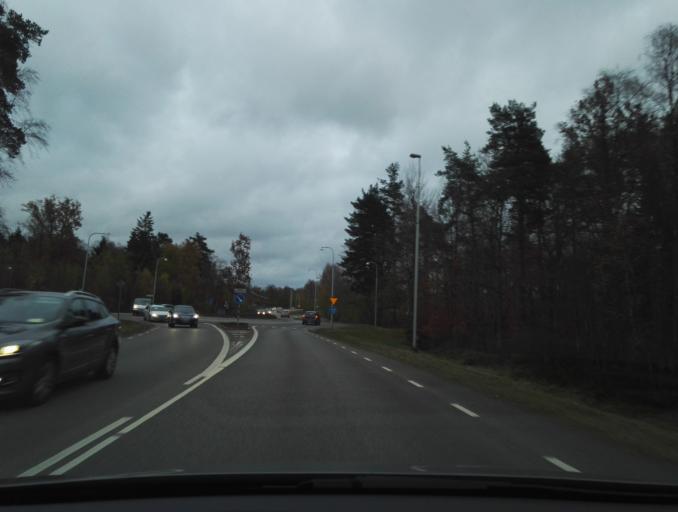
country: SE
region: Kronoberg
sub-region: Vaxjo Kommun
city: Vaexjoe
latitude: 56.8640
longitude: 14.7957
